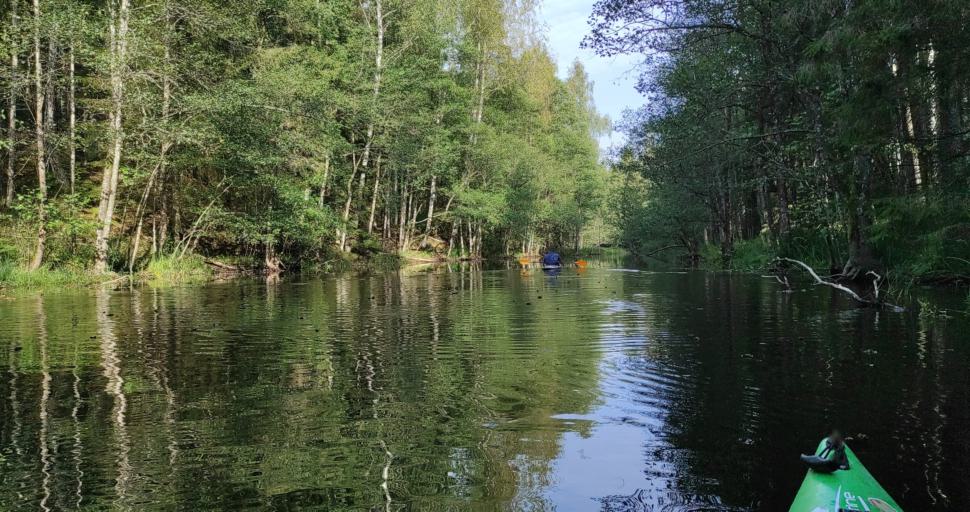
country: LV
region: Kuldigas Rajons
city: Kuldiga
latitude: 57.2251
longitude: 22.0852
